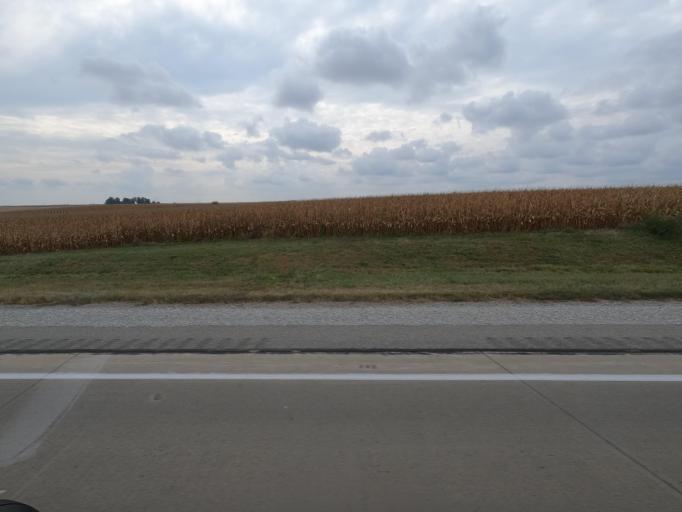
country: US
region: Iowa
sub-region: Jasper County
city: Monroe
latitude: 41.5605
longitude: -93.1510
